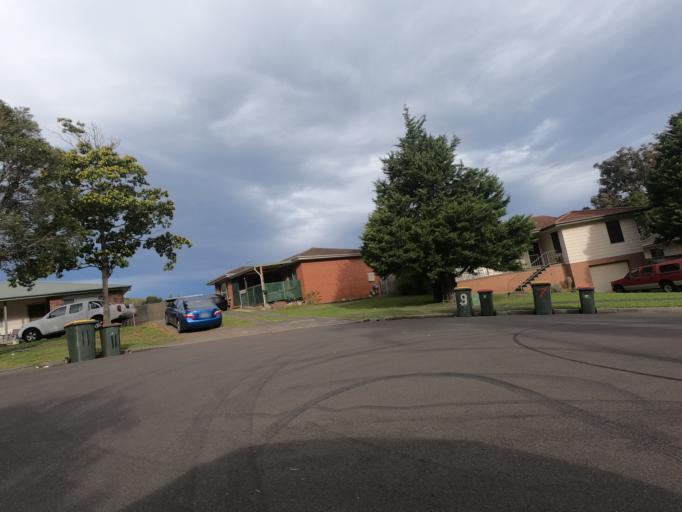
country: AU
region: New South Wales
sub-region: Wollongong
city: Berkeley
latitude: -34.4756
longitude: 150.8510
